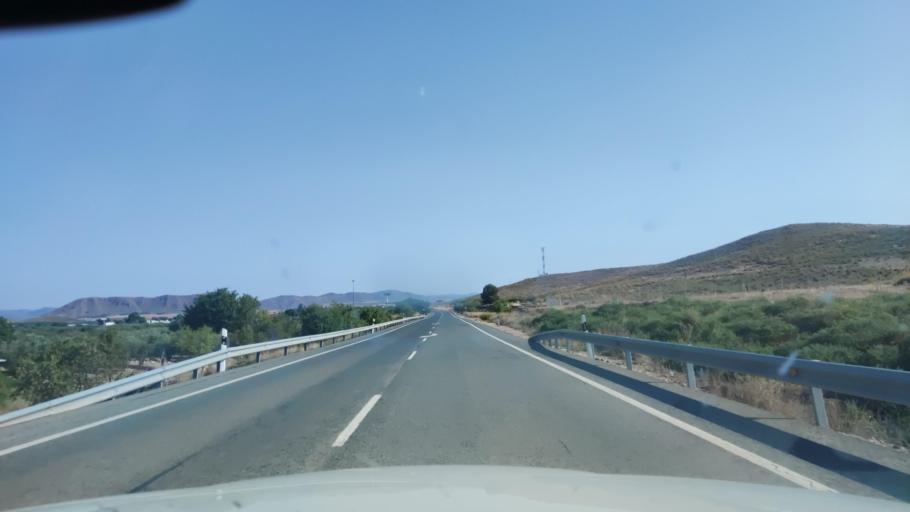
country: ES
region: Castille-La Mancha
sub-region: Provincia de Albacete
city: Tobarra
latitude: 38.6091
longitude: -1.6829
